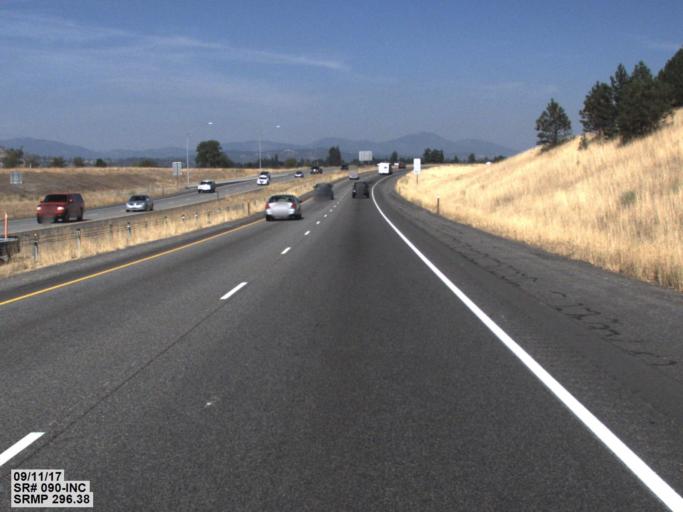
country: US
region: Washington
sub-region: Spokane County
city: Liberty Lake
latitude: 47.6748
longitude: -117.1064
